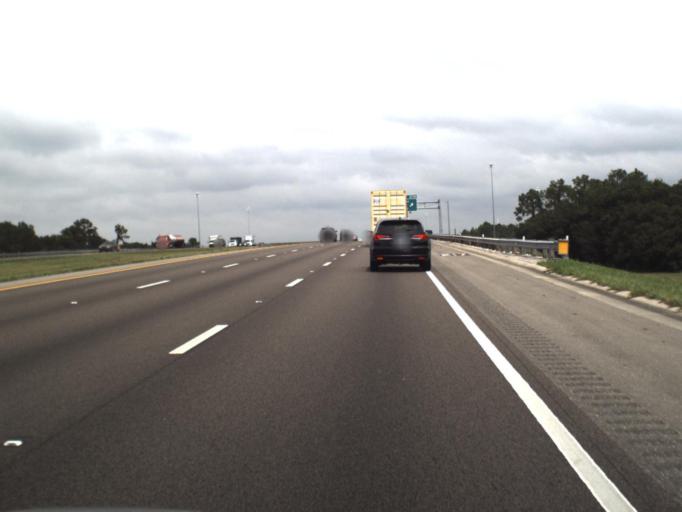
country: US
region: Florida
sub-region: Sarasota County
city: Desoto Lakes
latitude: 27.4385
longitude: -82.4592
